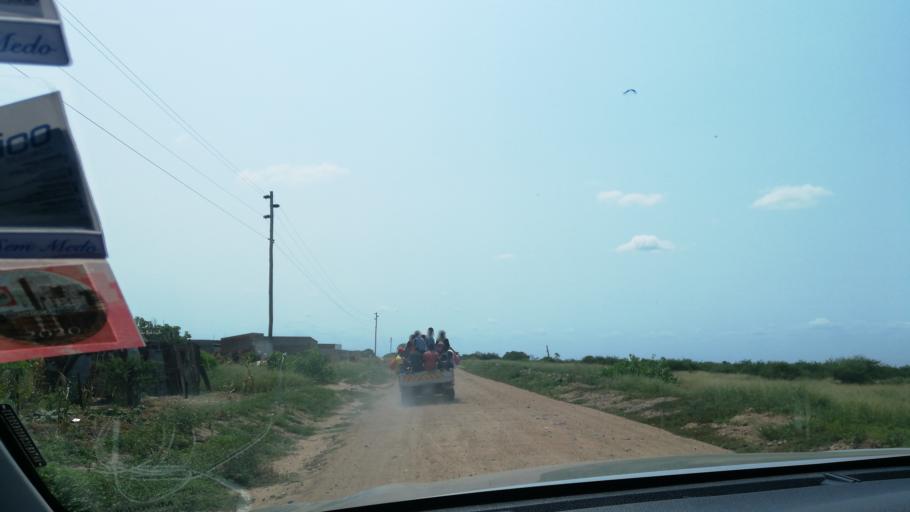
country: MZ
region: Maputo
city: Matola
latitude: -26.0637
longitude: 32.3902
